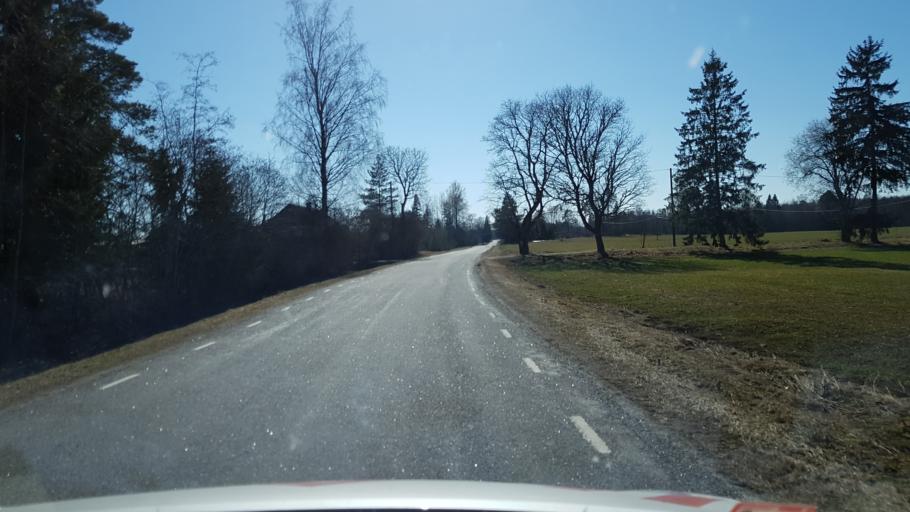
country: EE
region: Laeaene-Virumaa
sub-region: Tamsalu vald
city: Tamsalu
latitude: 59.0822
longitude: 26.1560
